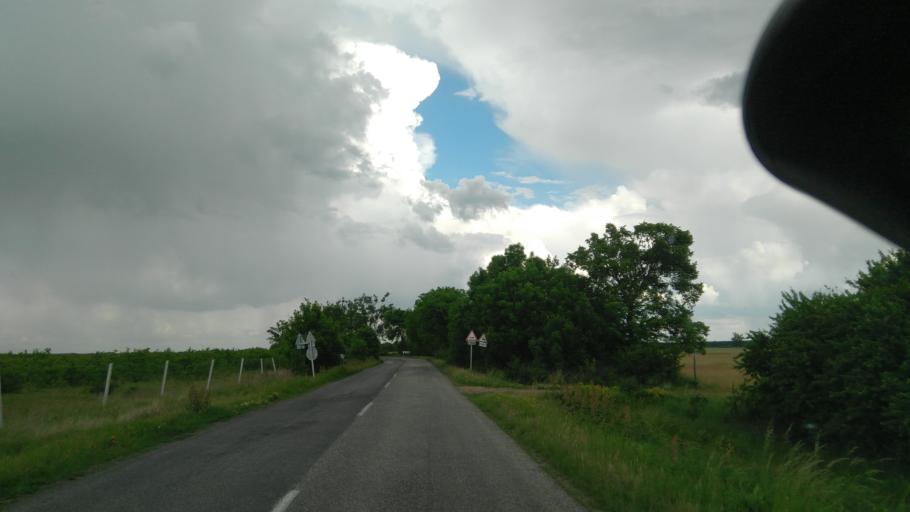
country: HU
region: Bekes
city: Fuzesgyarmat
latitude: 47.1505
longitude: 21.1263
